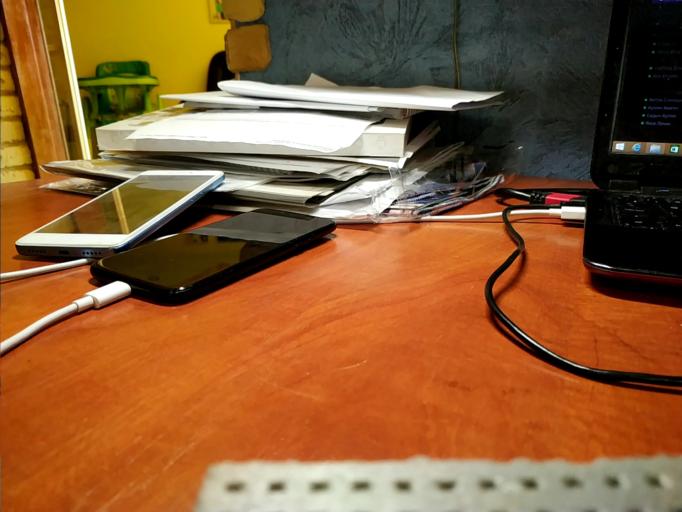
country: RU
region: Tverskaya
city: Spirovo
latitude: 57.4186
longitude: 35.1196
